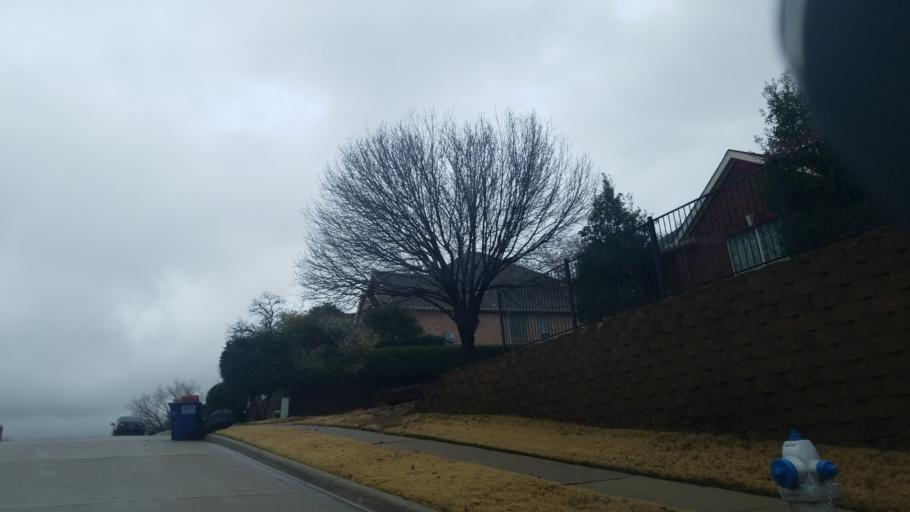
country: US
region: Texas
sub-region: Denton County
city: Corinth
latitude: 33.1450
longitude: -97.0893
